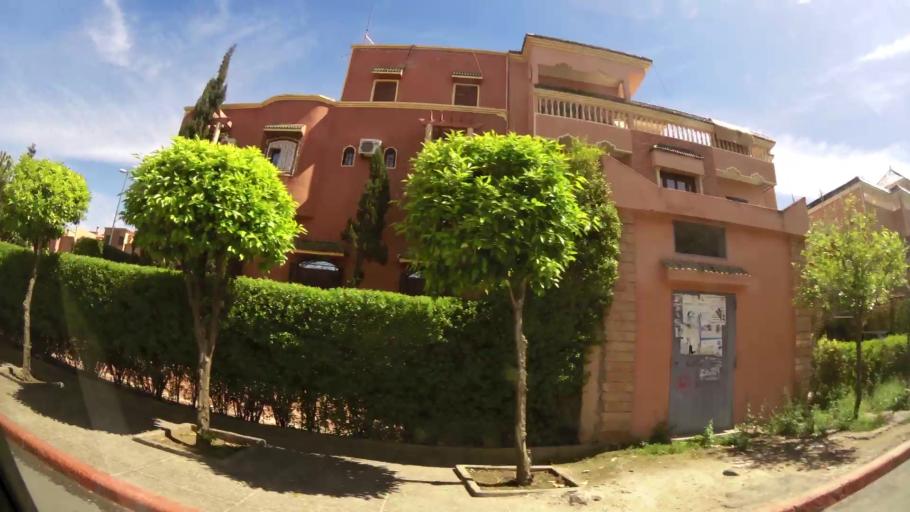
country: MA
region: Marrakech-Tensift-Al Haouz
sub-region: Marrakech
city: Marrakesh
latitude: 31.6653
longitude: -8.0076
